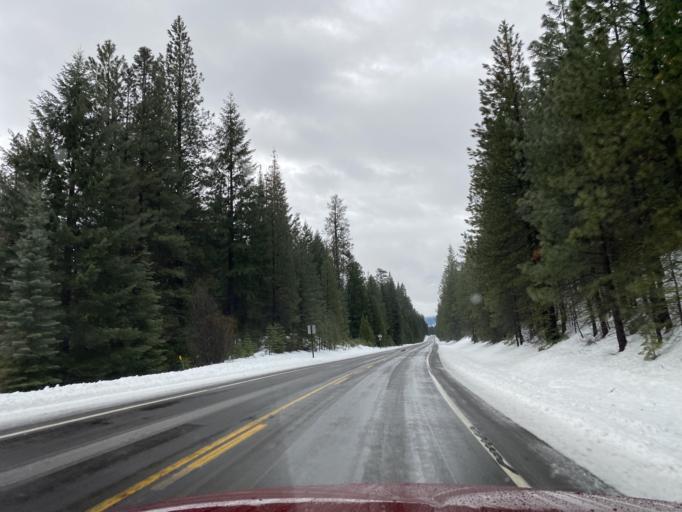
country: US
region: Oregon
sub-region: Klamath County
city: Klamath Falls
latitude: 42.5210
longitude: -122.0842
